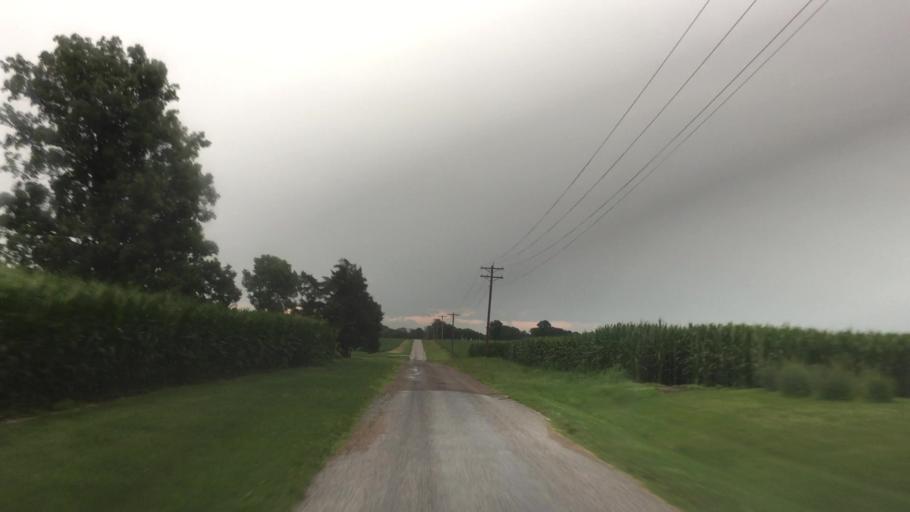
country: US
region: Illinois
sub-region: Hancock County
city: Nauvoo
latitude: 40.5495
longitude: -91.3632
